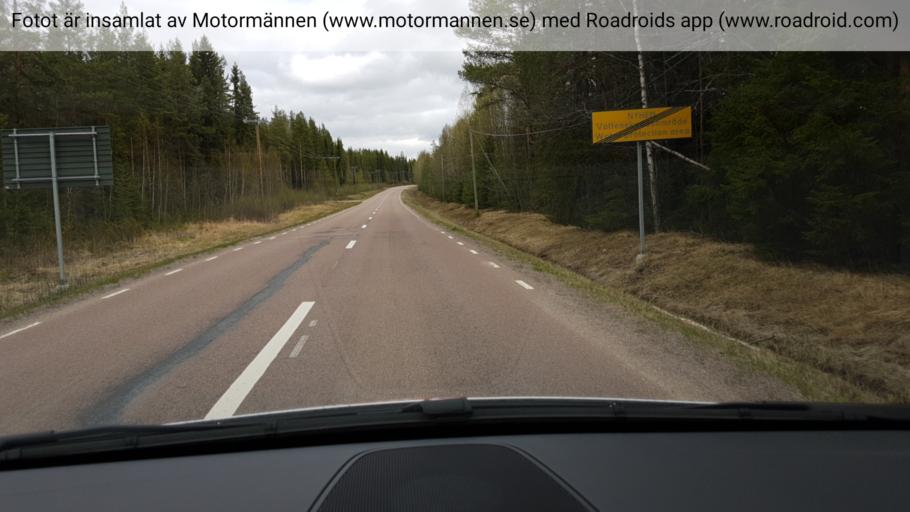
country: SE
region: Jaemtland
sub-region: Braecke Kommun
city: Braecke
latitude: 62.8986
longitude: 15.6300
